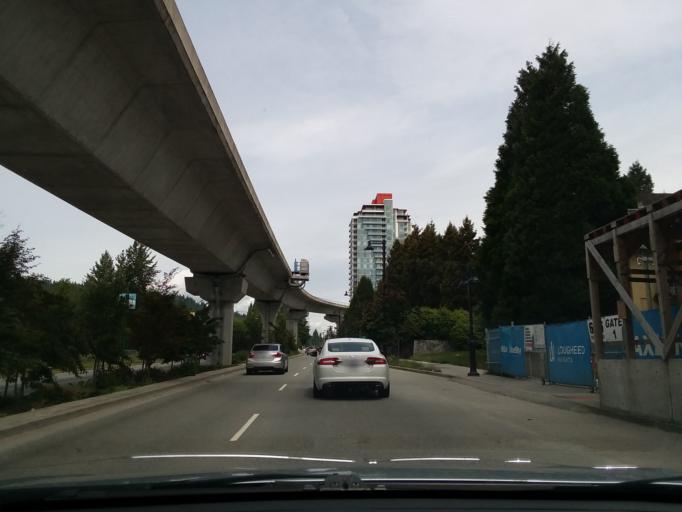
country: CA
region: British Columbia
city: Port Moody
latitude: 49.2573
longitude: -122.8928
